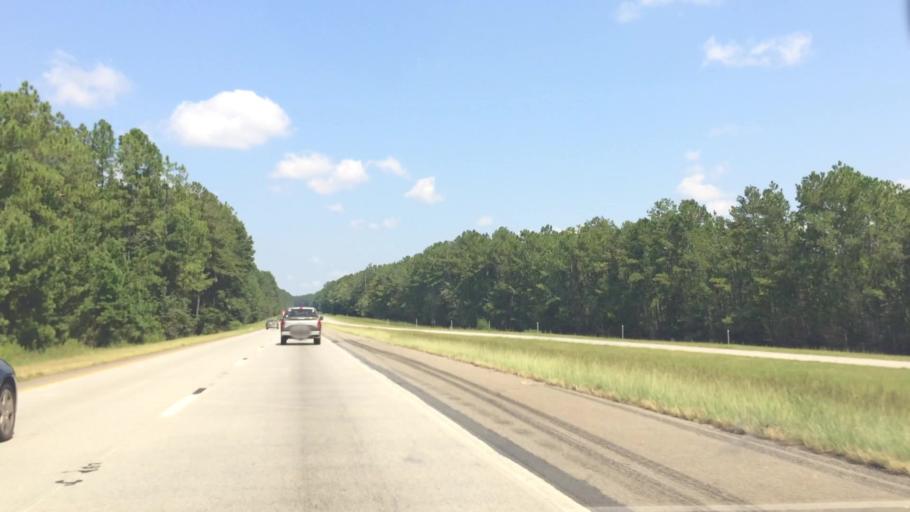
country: US
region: South Carolina
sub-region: Colleton County
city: Walterboro
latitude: 33.0047
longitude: -80.6685
